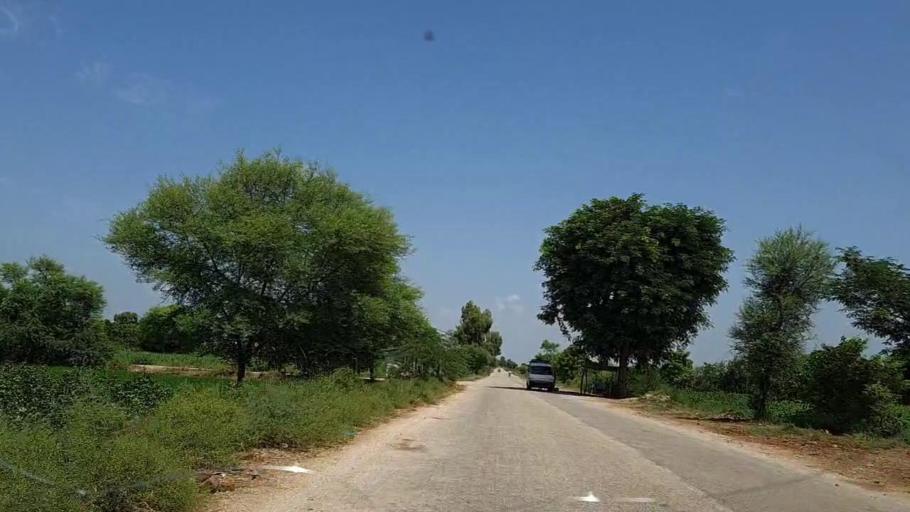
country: PK
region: Sindh
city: Pad Idan
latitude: 26.8017
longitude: 68.2226
